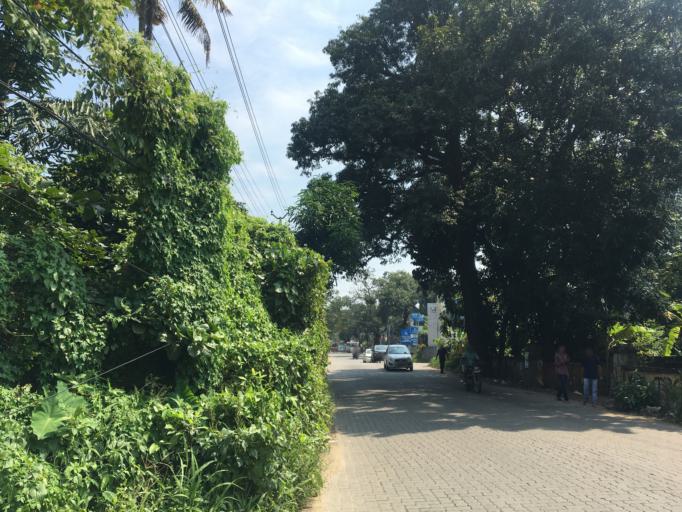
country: IN
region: Kerala
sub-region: Ernakulam
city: Cochin
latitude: 9.9622
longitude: 76.3202
